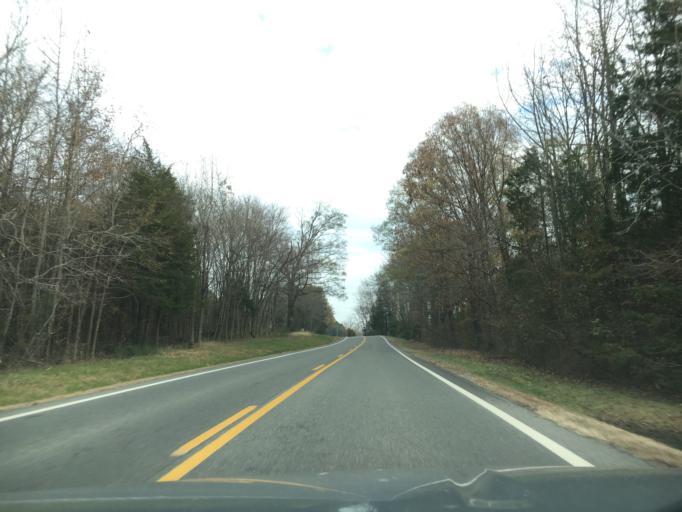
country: US
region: Virginia
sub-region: Cumberland County
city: Cumberland
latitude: 37.4573
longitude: -78.2980
